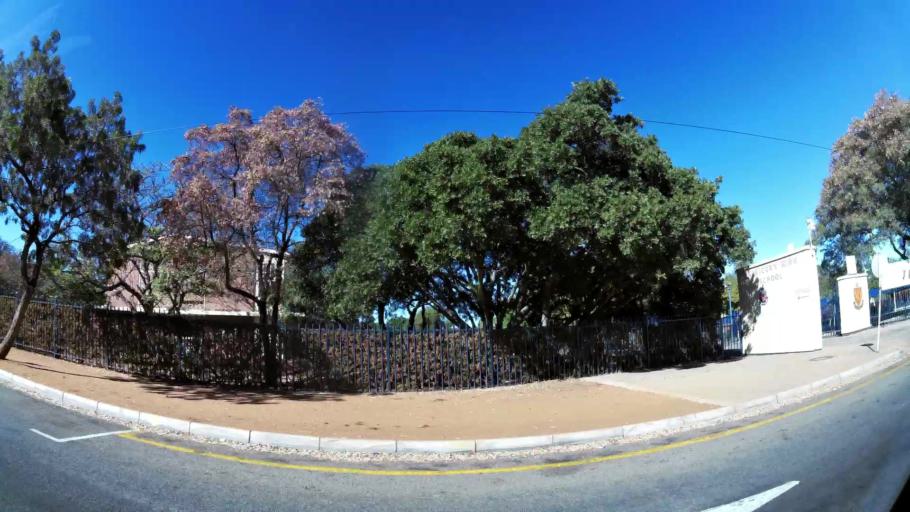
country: ZA
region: Limpopo
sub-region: Capricorn District Municipality
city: Polokwane
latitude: -23.9077
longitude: 29.4719
